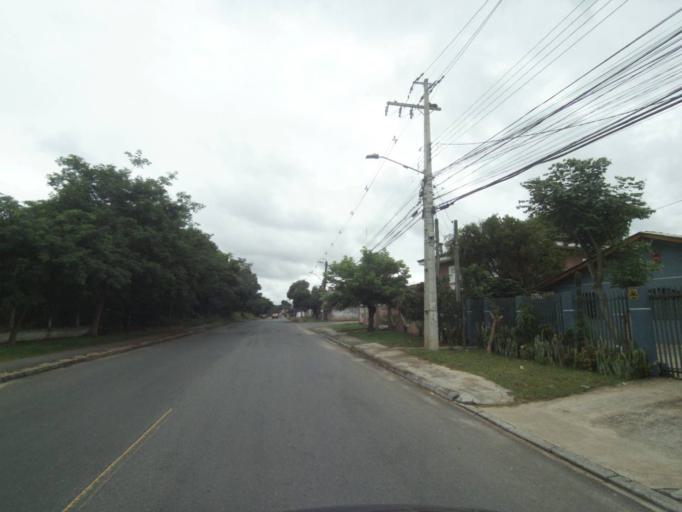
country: BR
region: Parana
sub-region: Curitiba
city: Curitiba
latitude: -25.4750
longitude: -49.3300
